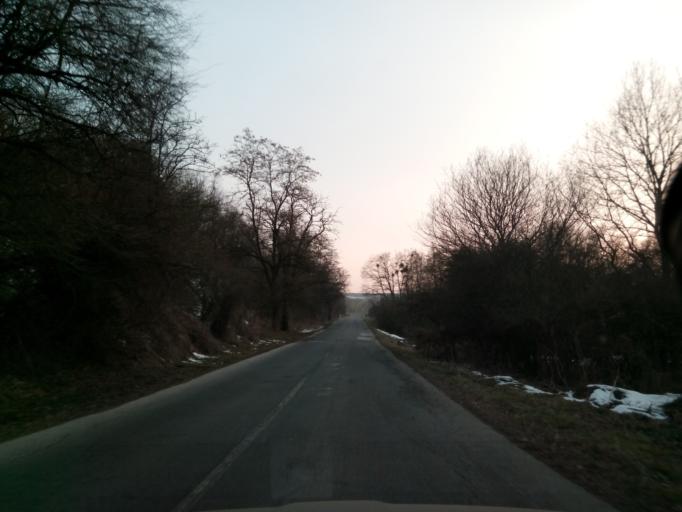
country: HU
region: Borsod-Abauj-Zemplen
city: Gonc
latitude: 48.5027
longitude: 21.3037
